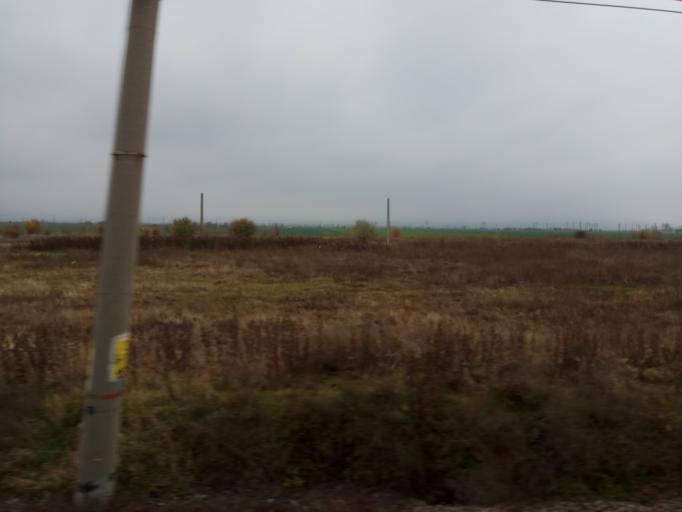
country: RO
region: Prahova
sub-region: Comuna Baba Ana
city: Conduratu
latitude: 44.9905
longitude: 26.4203
